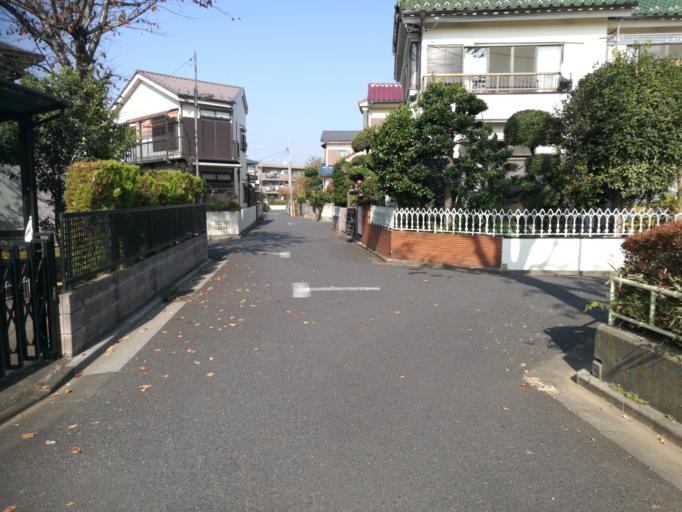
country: JP
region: Tokyo
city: Musashino
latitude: 35.7381
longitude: 139.5703
